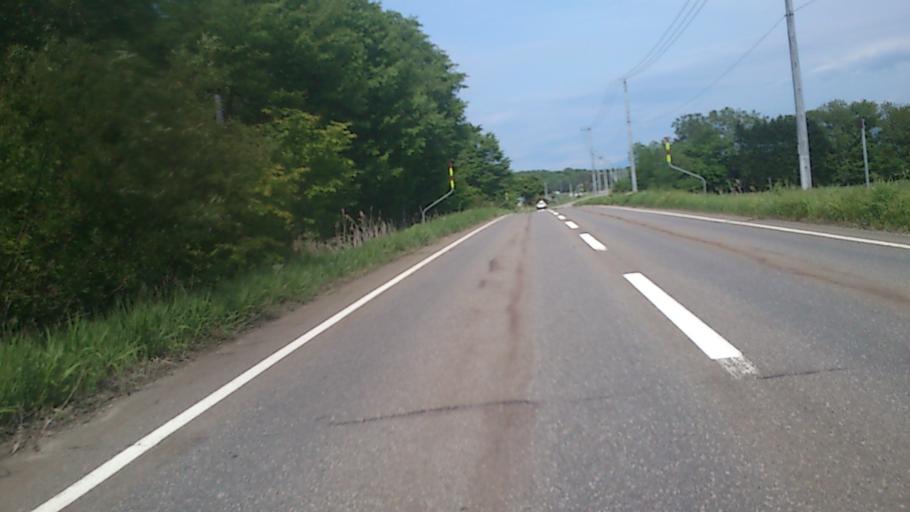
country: JP
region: Hokkaido
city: Otofuke
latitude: 43.2647
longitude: 143.5817
